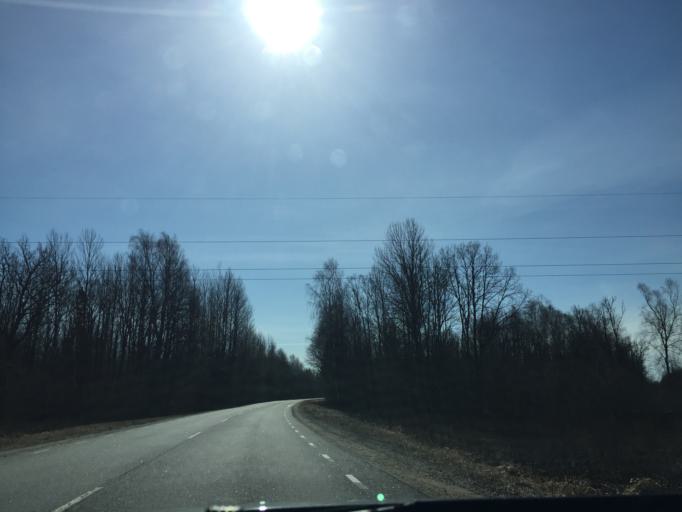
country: EE
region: Laeaene
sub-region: Lihula vald
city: Lihula
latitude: 58.6249
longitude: 23.6887
